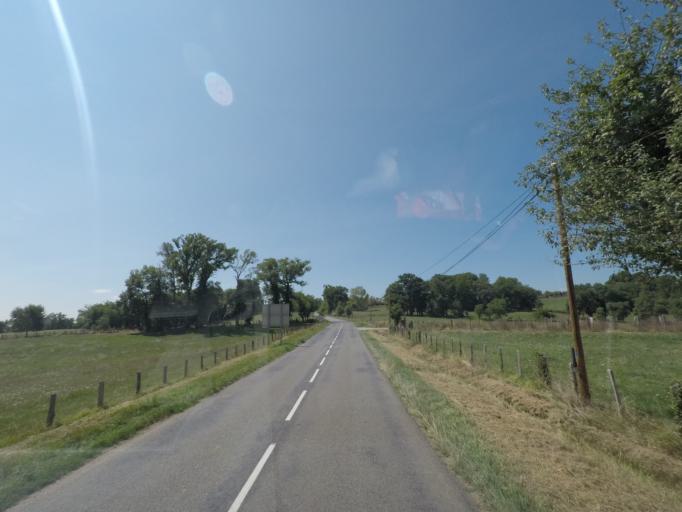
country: FR
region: Midi-Pyrenees
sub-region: Departement de l'Aveyron
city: Capdenac-Gare
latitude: 44.6206
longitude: 2.1136
